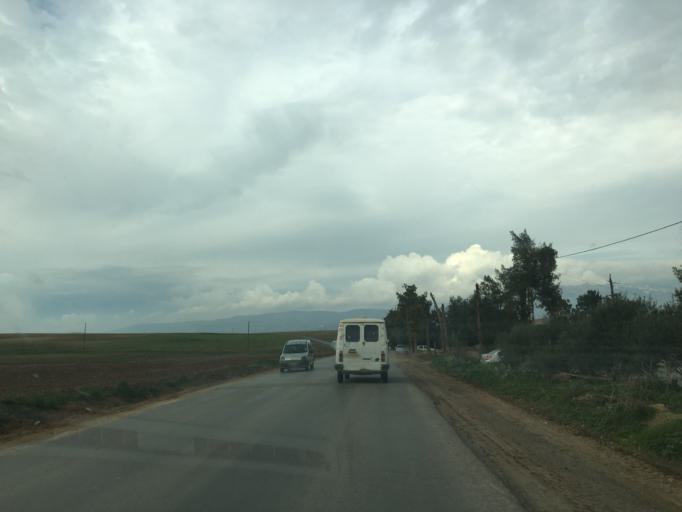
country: DZ
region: Bouira
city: Bouira
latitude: 36.3186
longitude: 3.8656
